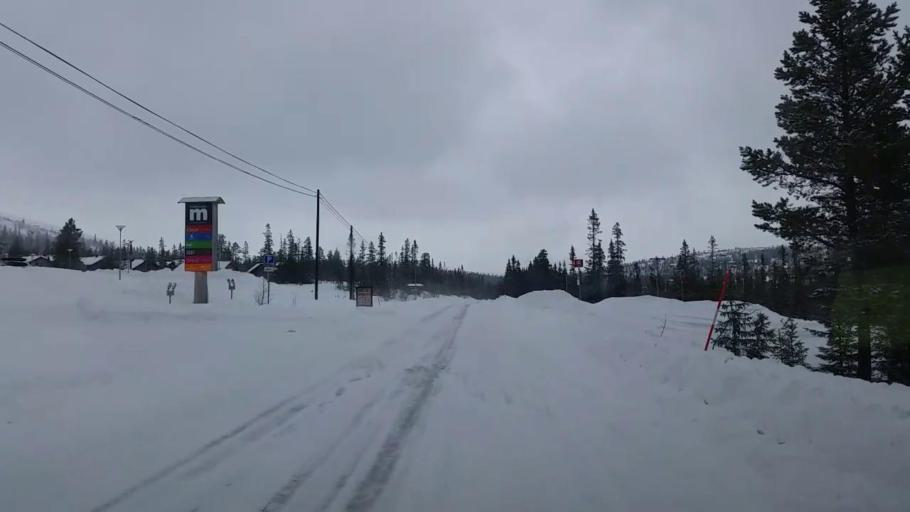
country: SE
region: Jaemtland
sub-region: Bergs Kommun
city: Hoverberg
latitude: 62.4943
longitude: 14.1145
